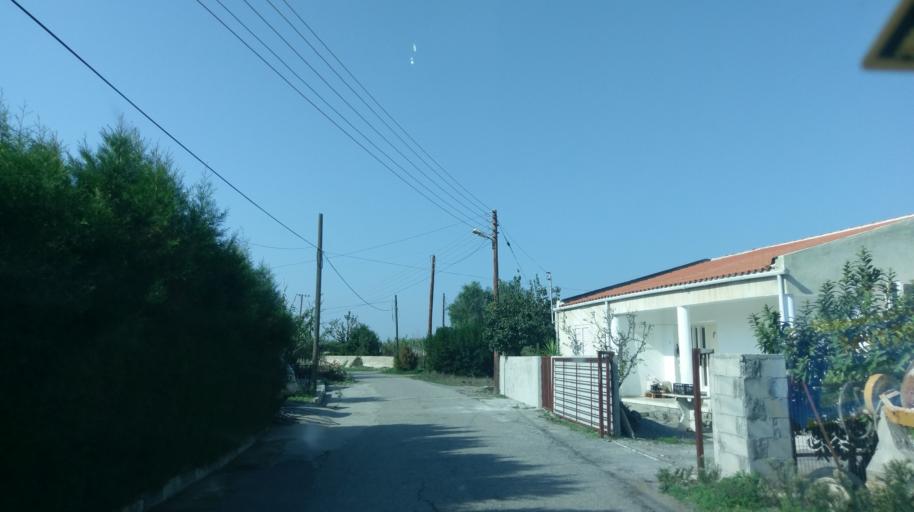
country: CY
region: Lefkosia
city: Morfou
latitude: 35.2258
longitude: 32.9372
